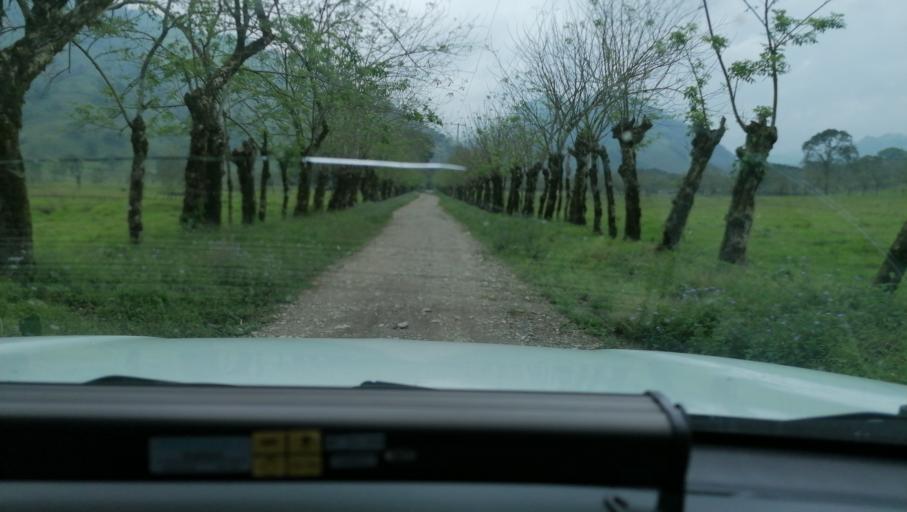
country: MX
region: Chiapas
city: Ixtacomitan
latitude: 17.3659
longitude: -93.1788
